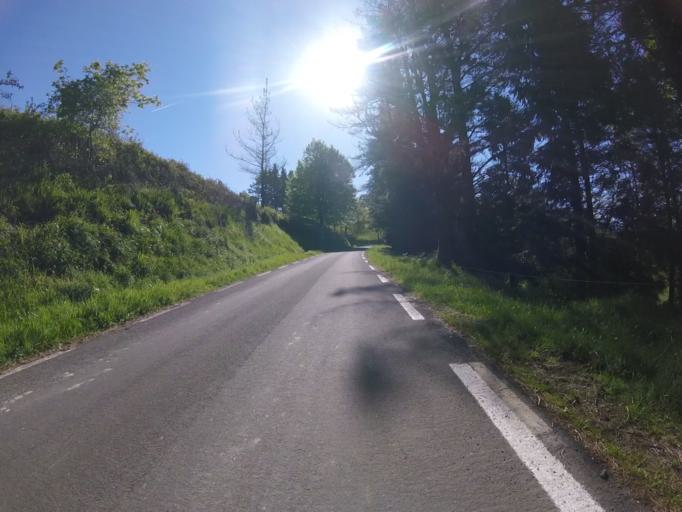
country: ES
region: Basque Country
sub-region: Provincia de Guipuzcoa
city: Aizarnazabal
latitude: 43.2164
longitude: -2.2106
